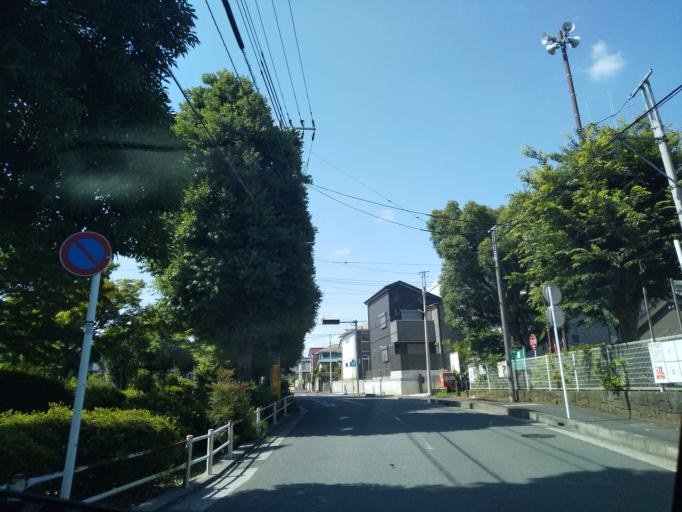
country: JP
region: Kanagawa
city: Zama
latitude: 35.4594
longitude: 139.4168
